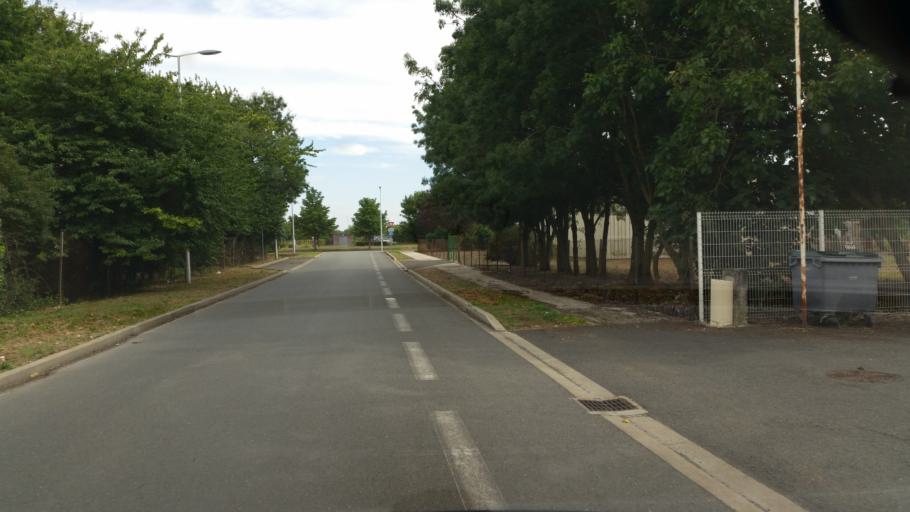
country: FR
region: Poitou-Charentes
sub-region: Departement de la Charente-Maritime
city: Surgeres
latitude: 46.1095
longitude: -0.7703
